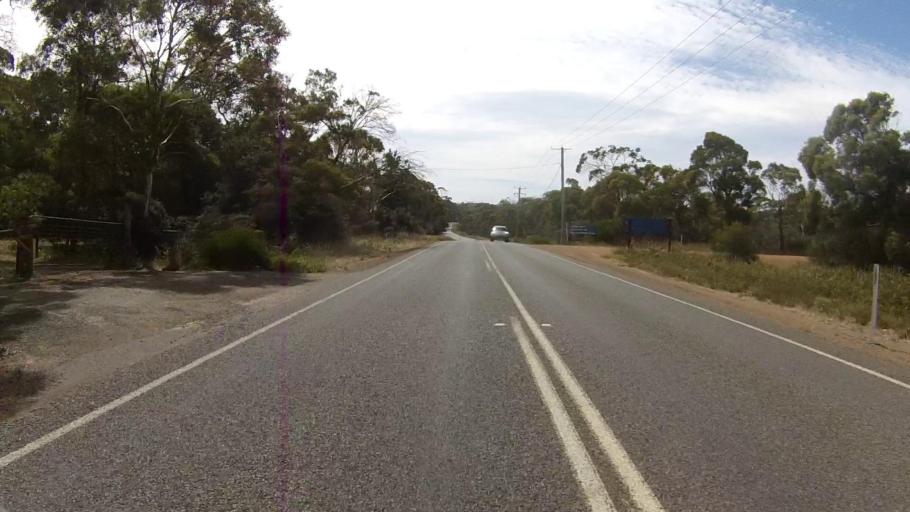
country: AU
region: Tasmania
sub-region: Clarence
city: Sandford
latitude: -43.0217
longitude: 147.4877
